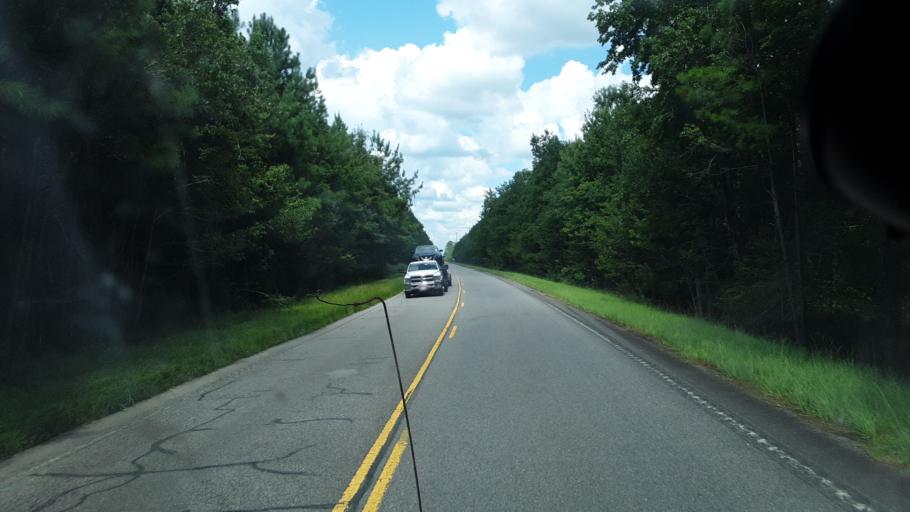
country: US
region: South Carolina
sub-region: Williamsburg County
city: Andrews
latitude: 33.5609
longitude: -79.4548
